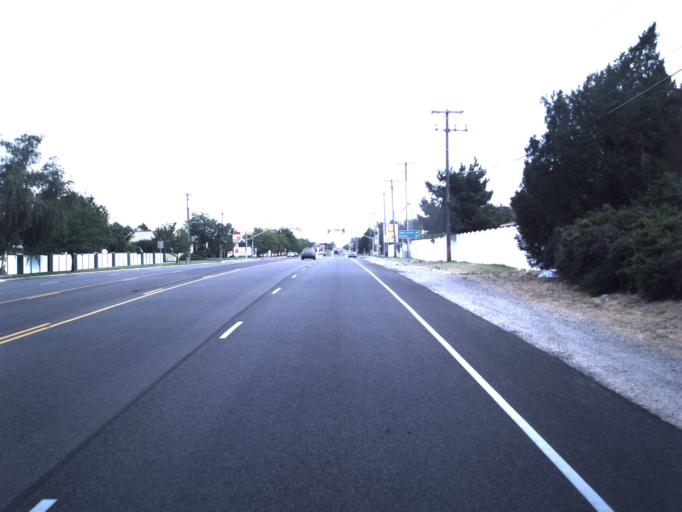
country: US
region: Utah
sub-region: Weber County
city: West Haven
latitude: 41.1929
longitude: -112.0259
